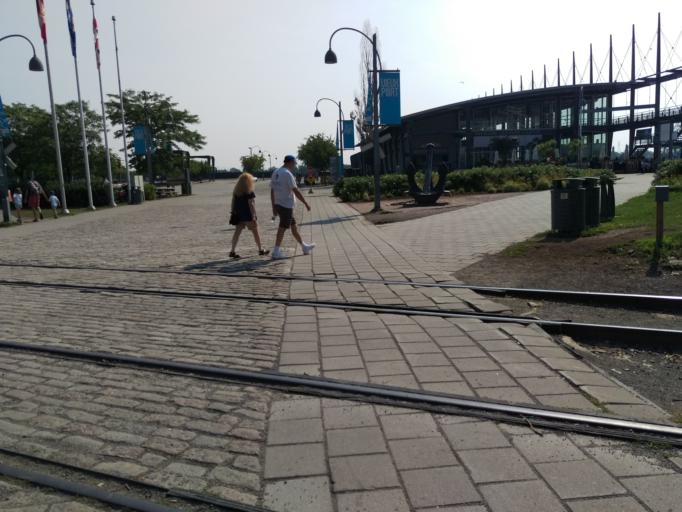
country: CA
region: Quebec
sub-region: Montreal
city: Montreal
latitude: 45.5072
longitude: -73.5518
